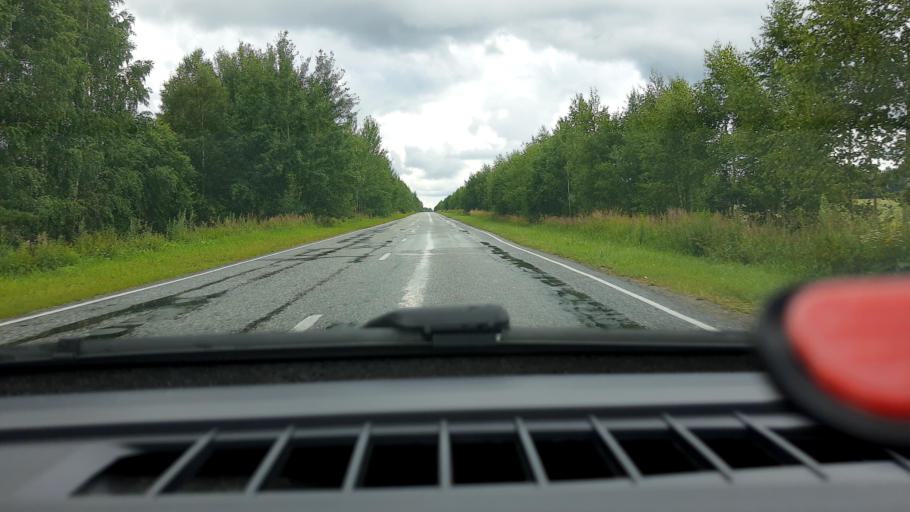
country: RU
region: Nizjnij Novgorod
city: Neklyudovo
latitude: 56.5175
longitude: 43.9179
